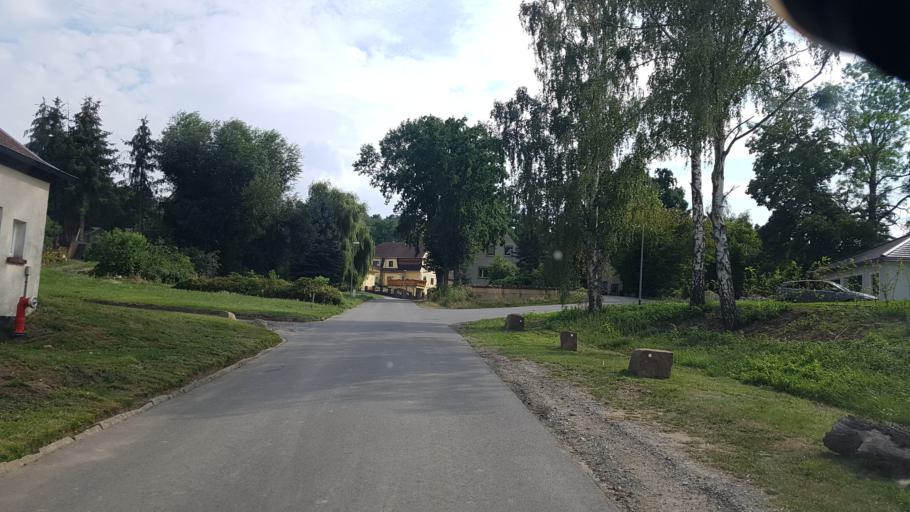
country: DE
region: Brandenburg
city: Grosskmehlen
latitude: 51.3739
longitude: 13.7232
